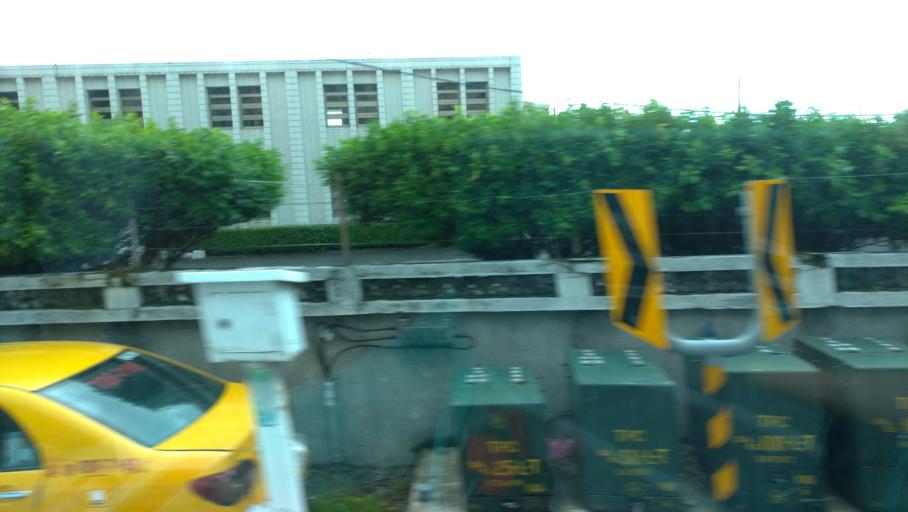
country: TW
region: Taiwan
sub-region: Keelung
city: Keelung
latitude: 25.1486
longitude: 121.7623
